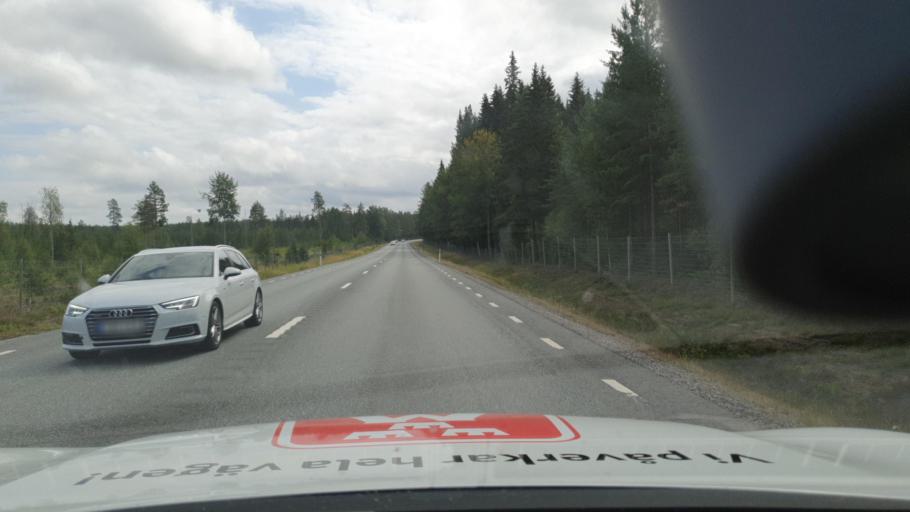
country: SE
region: Vaesterbotten
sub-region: Skelleftea Kommun
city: Burea
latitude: 64.5896
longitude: 21.2149
